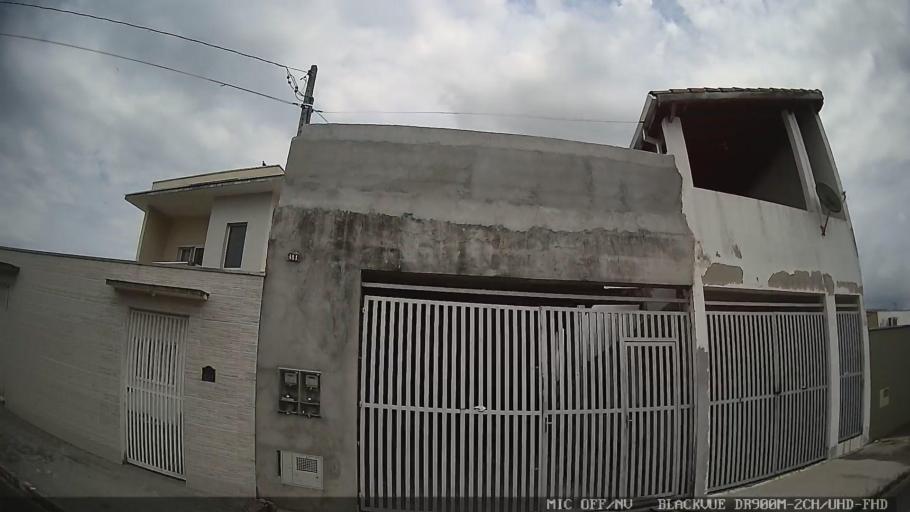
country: BR
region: Sao Paulo
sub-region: Caraguatatuba
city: Caraguatatuba
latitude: -23.6715
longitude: -45.4428
